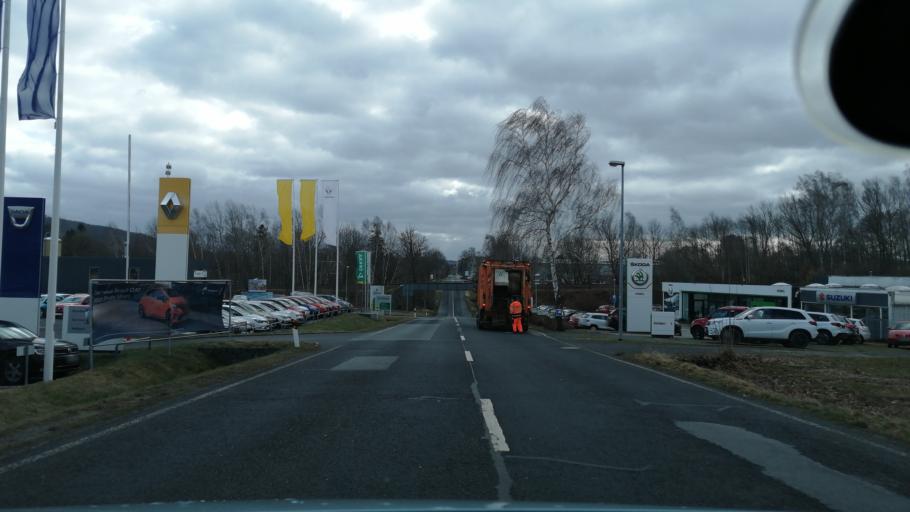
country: DE
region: Saxony
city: Lobau
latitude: 51.1043
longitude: 14.6541
